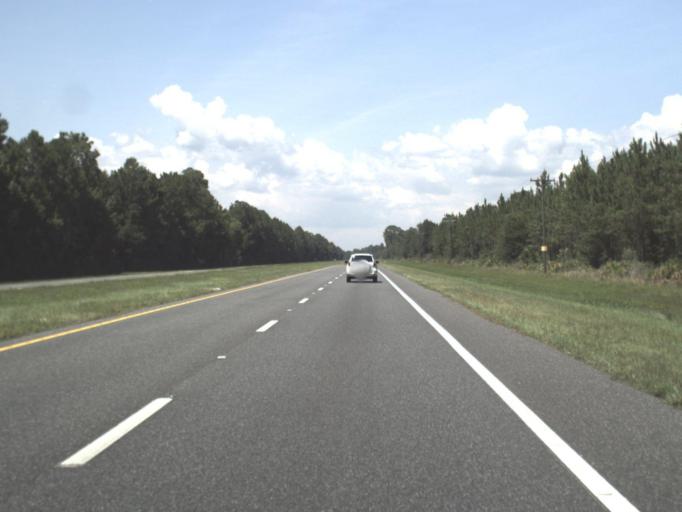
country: US
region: Florida
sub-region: Levy County
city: Inglis
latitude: 29.0750
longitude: -82.6434
